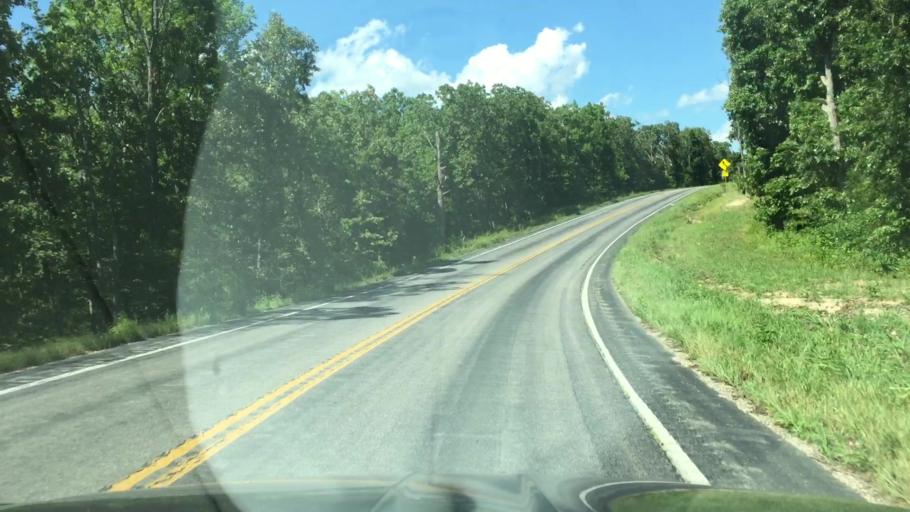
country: US
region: Missouri
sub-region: Miller County
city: Tuscumbia
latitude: 38.0939
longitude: -92.4988
